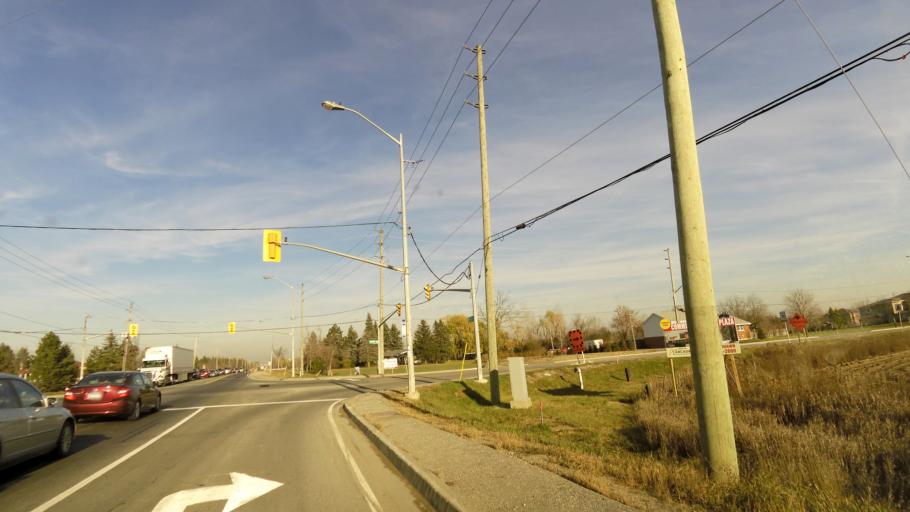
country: CA
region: Ontario
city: Brampton
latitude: 43.8003
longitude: -79.7491
